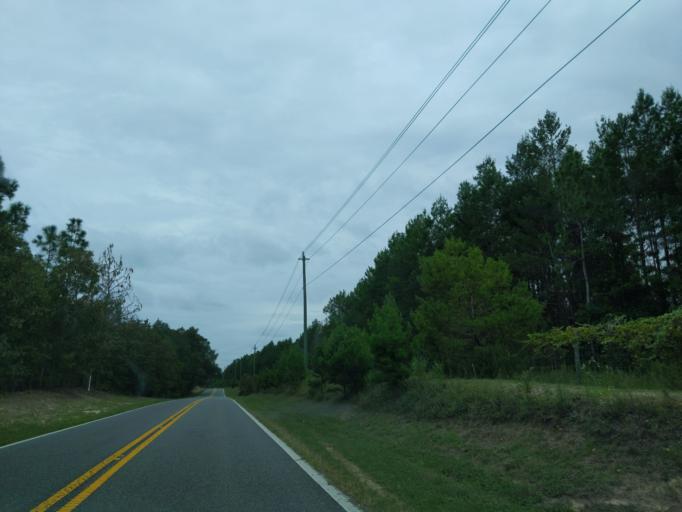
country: US
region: Florida
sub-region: Leon County
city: Woodville
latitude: 30.3696
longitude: -84.1842
